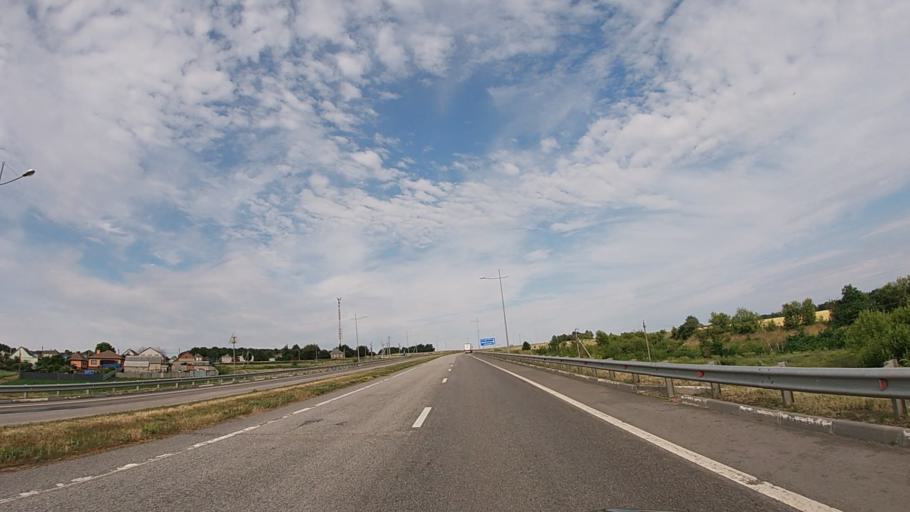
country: RU
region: Belgorod
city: Tomarovka
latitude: 50.7067
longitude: 36.2009
